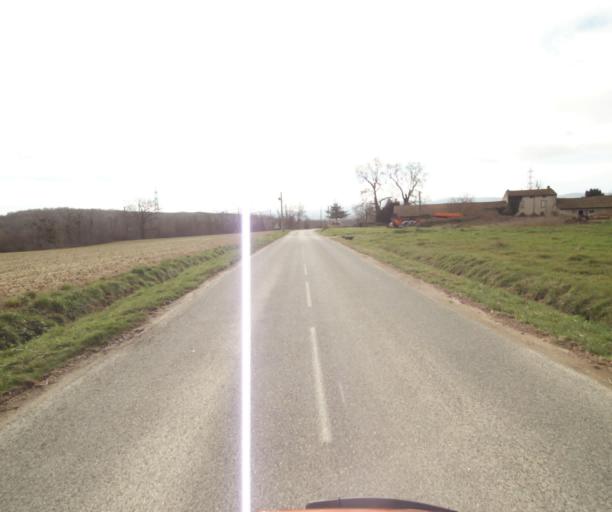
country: FR
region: Midi-Pyrenees
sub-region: Departement de l'Ariege
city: Pamiers
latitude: 43.1204
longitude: 1.5487
